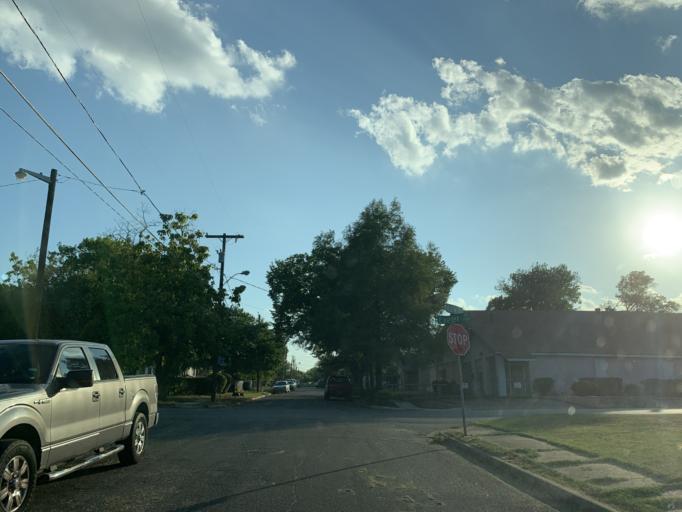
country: US
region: Texas
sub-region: Dallas County
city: Dallas
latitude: 32.7043
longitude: -96.7848
